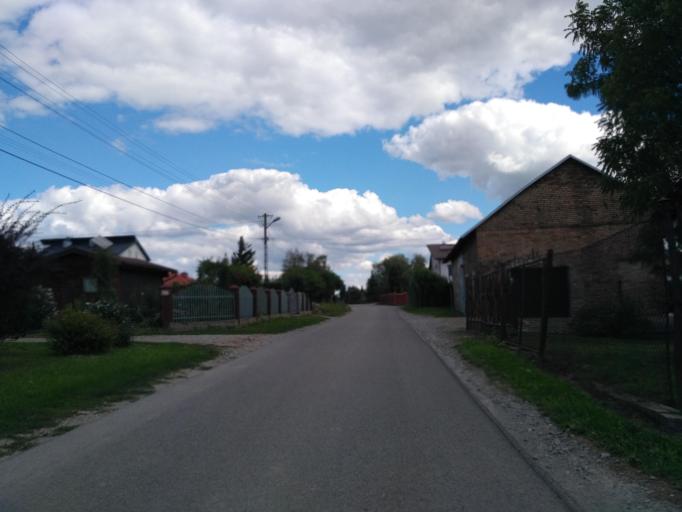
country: PL
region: Subcarpathian Voivodeship
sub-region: Powiat jasielski
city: Jaslo
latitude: 49.7627
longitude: 21.5209
